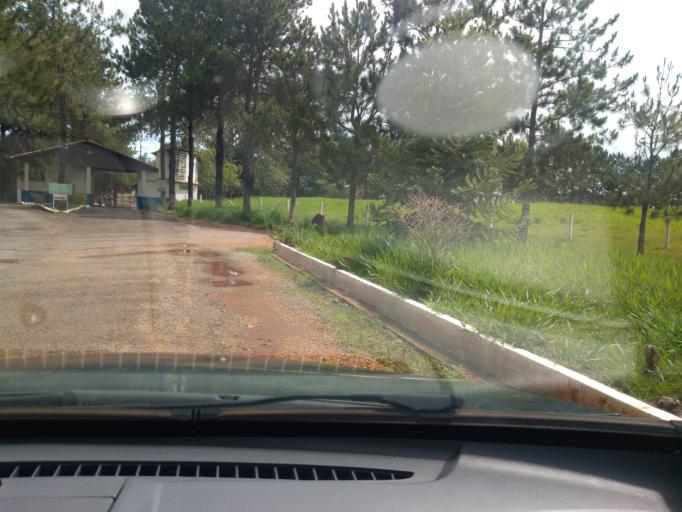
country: BR
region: Minas Gerais
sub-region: Tres Coracoes
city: Tres Coracoes
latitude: -21.7013
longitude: -45.2719
